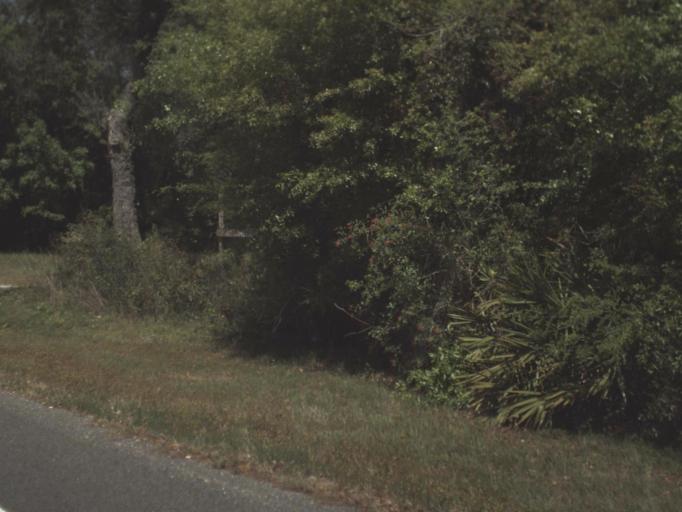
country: US
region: Florida
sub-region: Escambia County
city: Myrtle Grove
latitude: 30.3980
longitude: -87.4180
